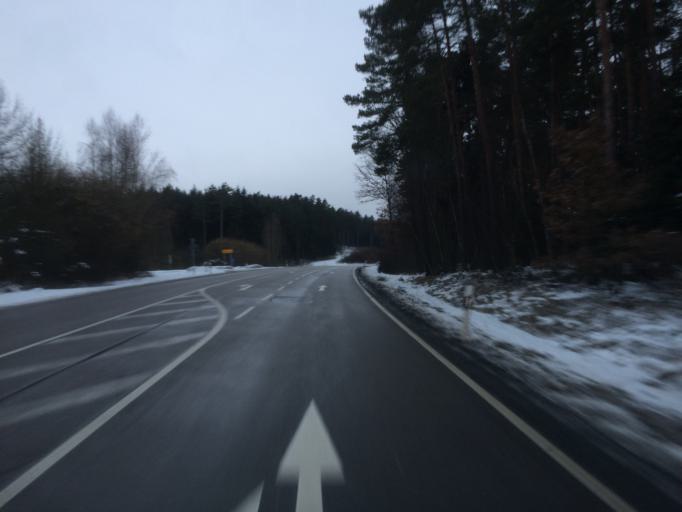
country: DE
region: Bavaria
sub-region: Upper Palatinate
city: Breitenbrunn
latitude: 49.3614
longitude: 12.0498
